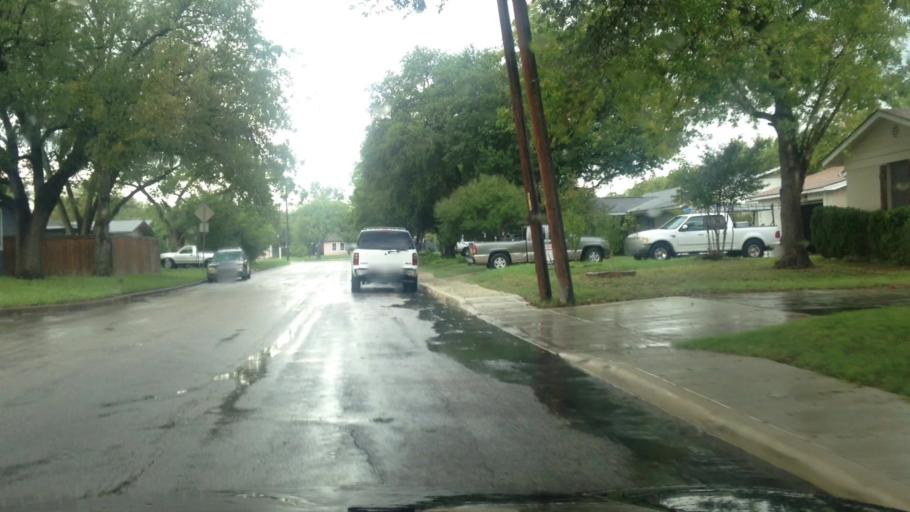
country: US
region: Texas
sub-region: Bexar County
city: Balcones Heights
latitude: 29.4821
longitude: -98.5472
